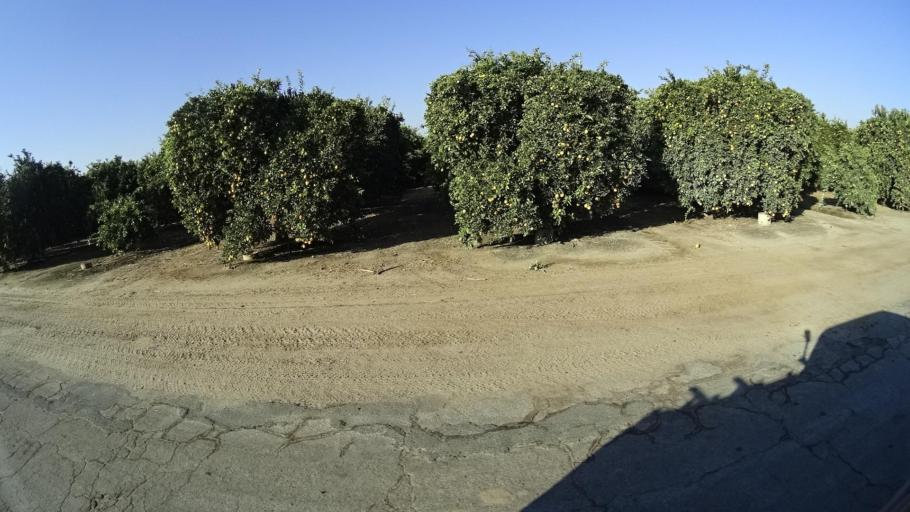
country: US
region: California
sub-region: Tulare County
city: Richgrove
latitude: 35.7735
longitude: -119.1607
